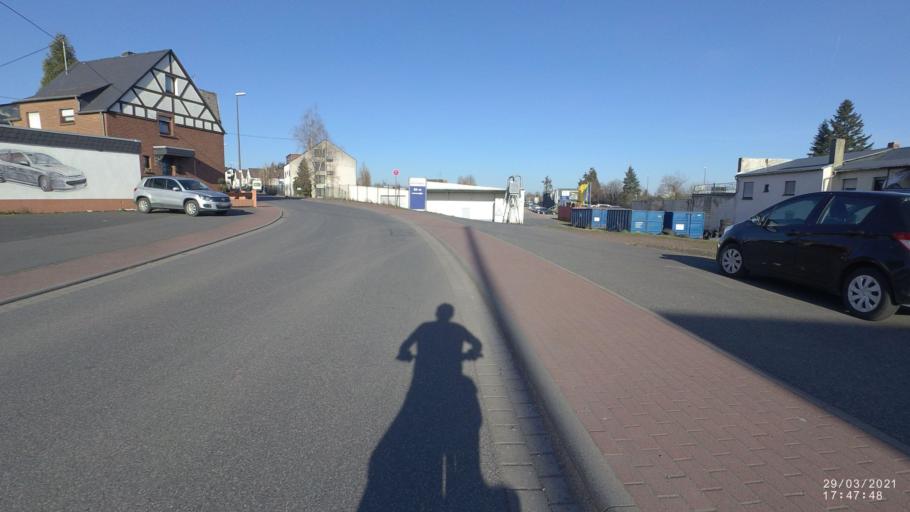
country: DE
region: Rheinland-Pfalz
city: Plaidt
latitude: 50.3966
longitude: 7.3915
